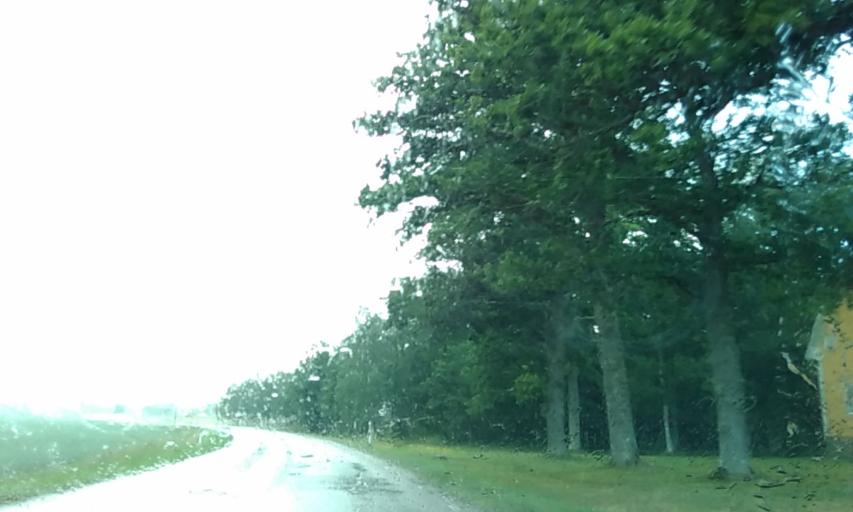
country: SE
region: Vaestra Goetaland
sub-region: Lidkopings Kommun
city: Lidkoping
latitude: 58.5035
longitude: 12.9413
